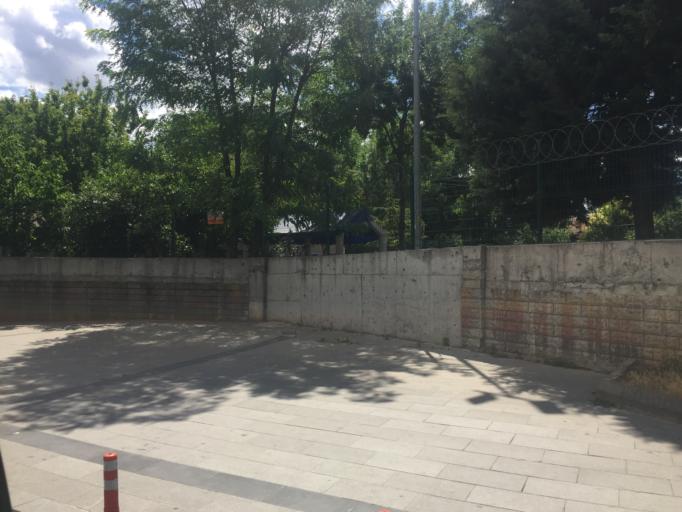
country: TR
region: Istanbul
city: merter keresteciler
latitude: 41.0333
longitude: 28.9124
